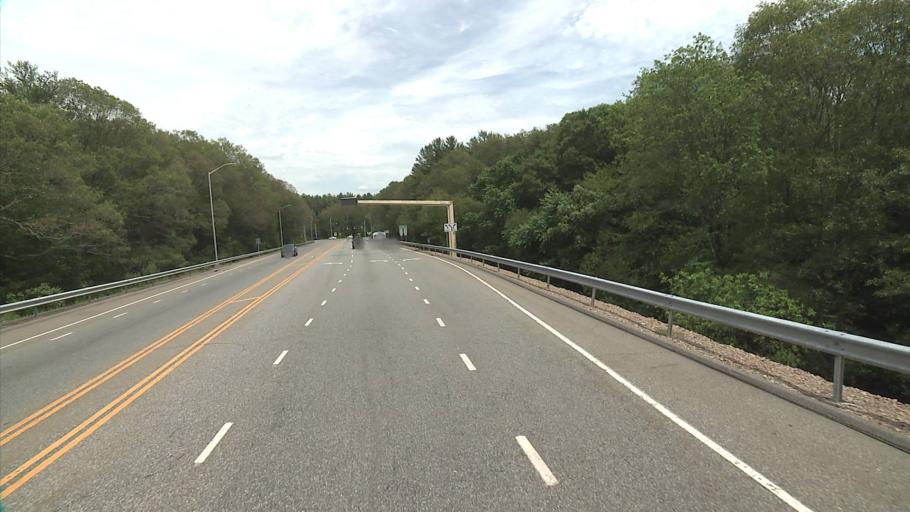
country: US
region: Connecticut
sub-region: New London County
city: Norwich
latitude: 41.4822
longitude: -72.0688
